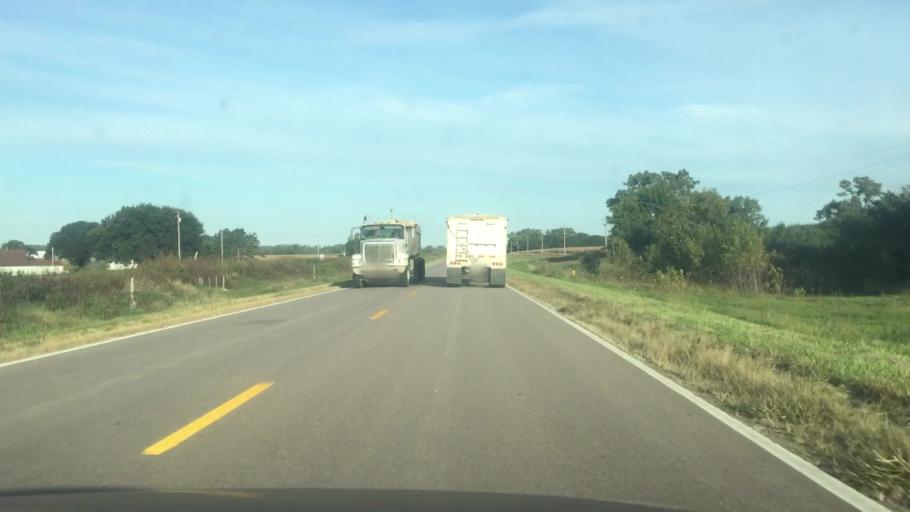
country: US
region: Nebraska
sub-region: Jefferson County
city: Fairbury
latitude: 40.0518
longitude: -97.0318
